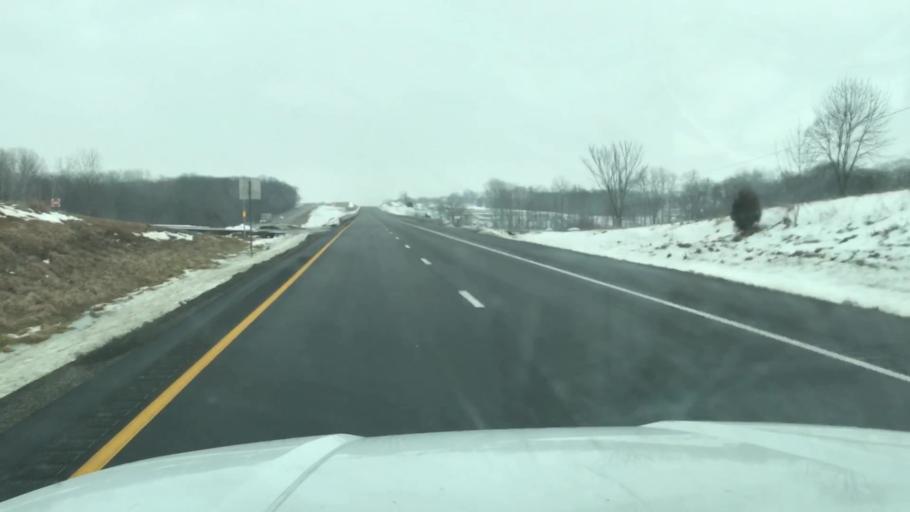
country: US
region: Missouri
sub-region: DeKalb County
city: Maysville
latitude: 39.7620
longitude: -94.4731
